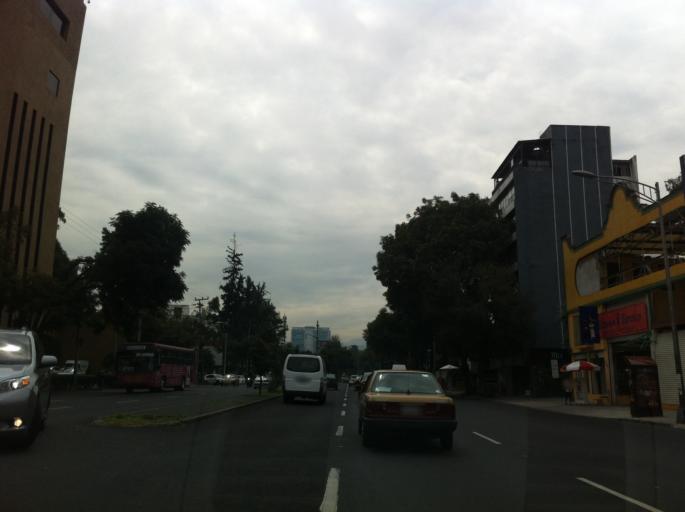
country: MX
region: Mexico City
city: Alvaro Obregon
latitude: 19.3530
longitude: -99.1903
